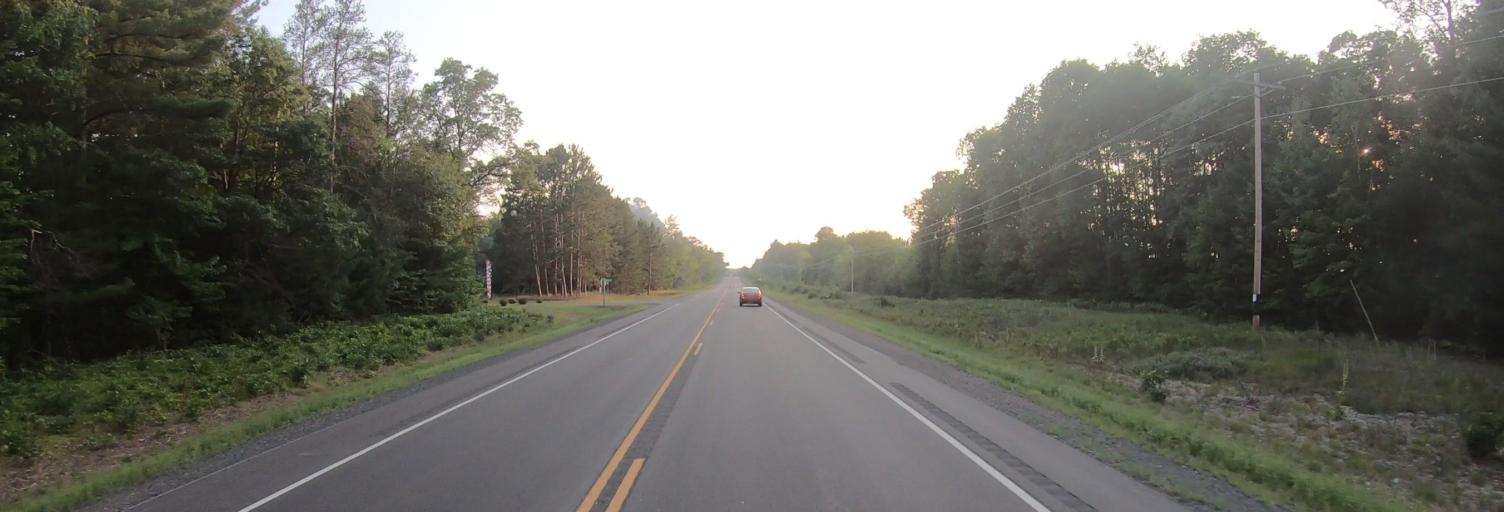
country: US
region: Wisconsin
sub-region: Burnett County
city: Siren
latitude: 45.8261
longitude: -92.3051
